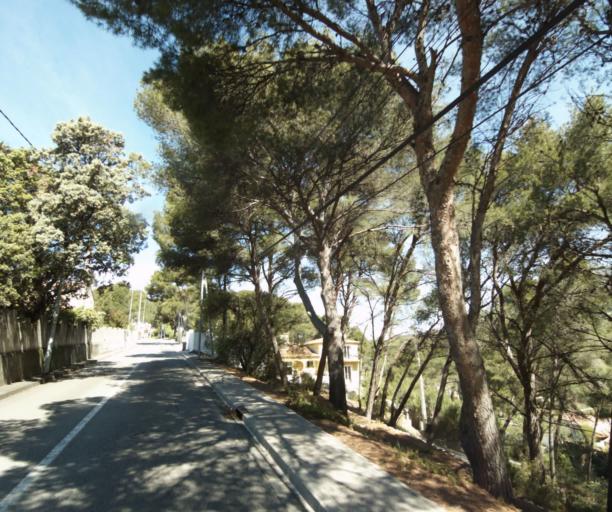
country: FR
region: Provence-Alpes-Cote d'Azur
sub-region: Departement des Bouches-du-Rhone
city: Rognac
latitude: 43.5149
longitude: 5.2134
